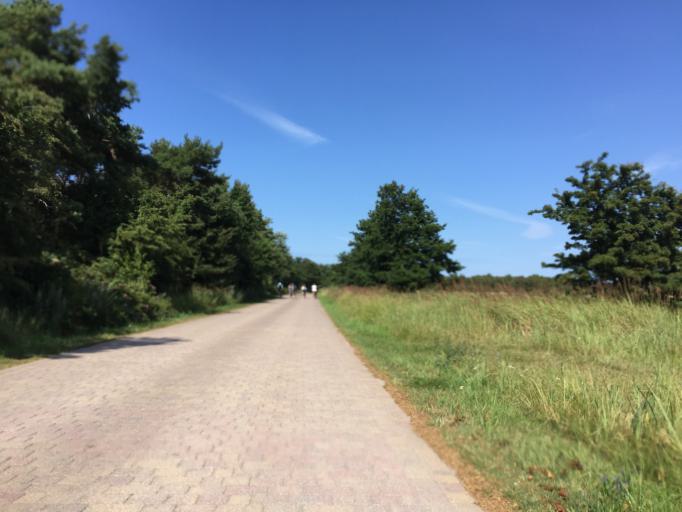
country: DE
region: Mecklenburg-Vorpommern
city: Hiddensee
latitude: 54.5305
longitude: 13.0863
